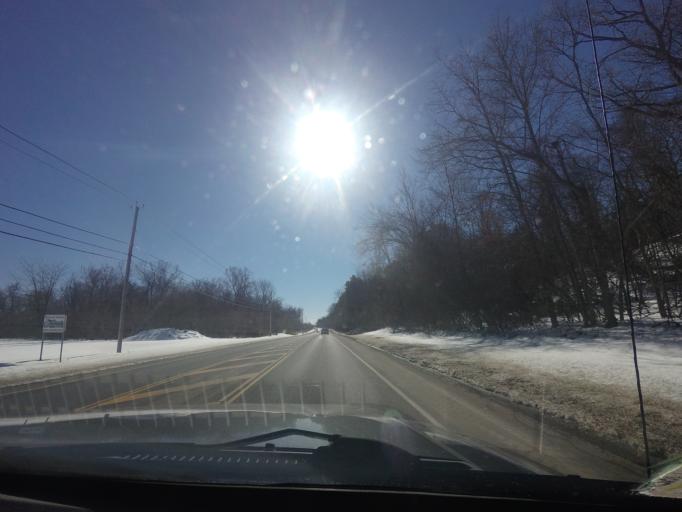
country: US
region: New York
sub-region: Saratoga County
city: Waterford
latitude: 42.7778
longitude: -73.6573
